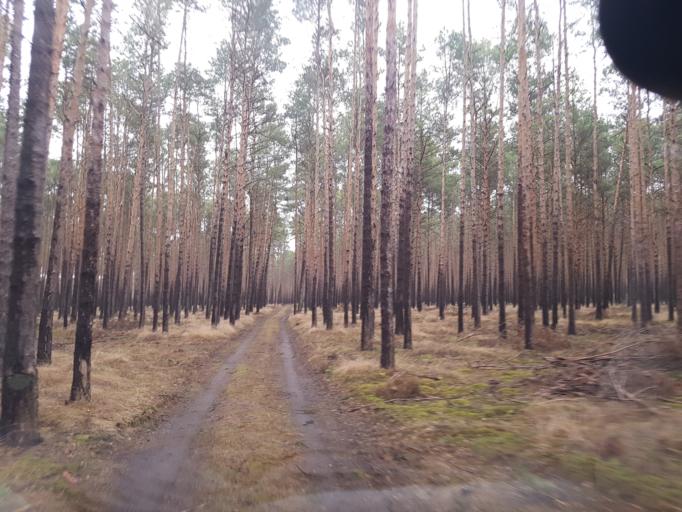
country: DE
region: Brandenburg
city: Finsterwalde
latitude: 51.5731
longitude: 13.6868
